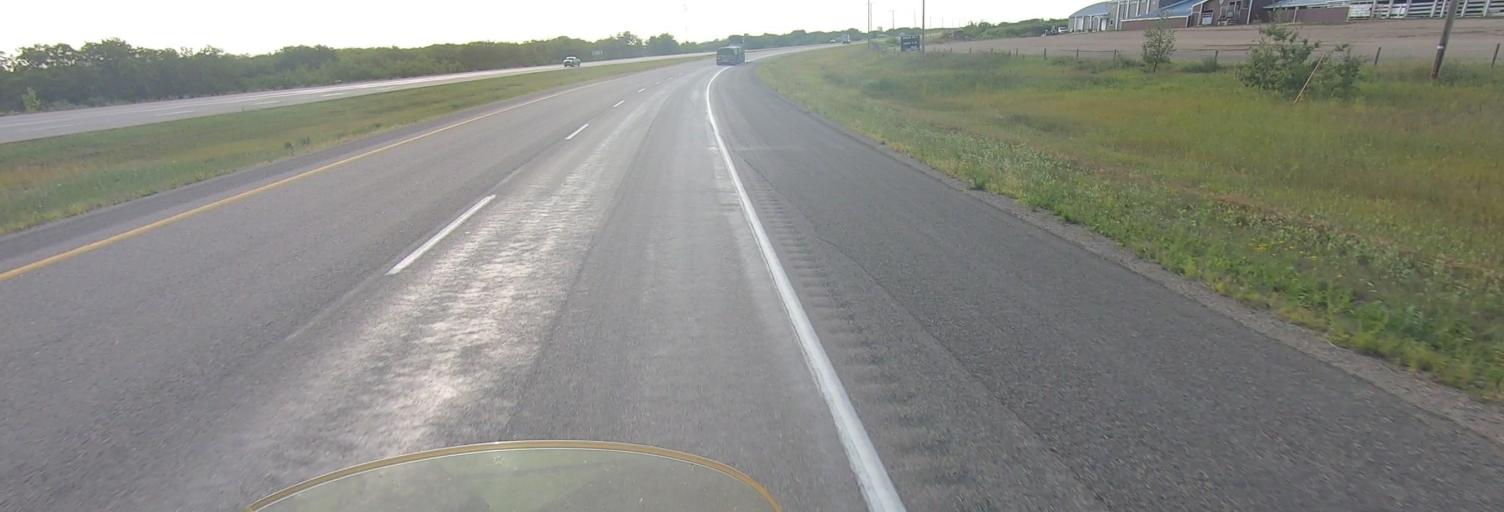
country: CA
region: Saskatchewan
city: Esterhazy
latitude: 50.3378
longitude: -102.2843
